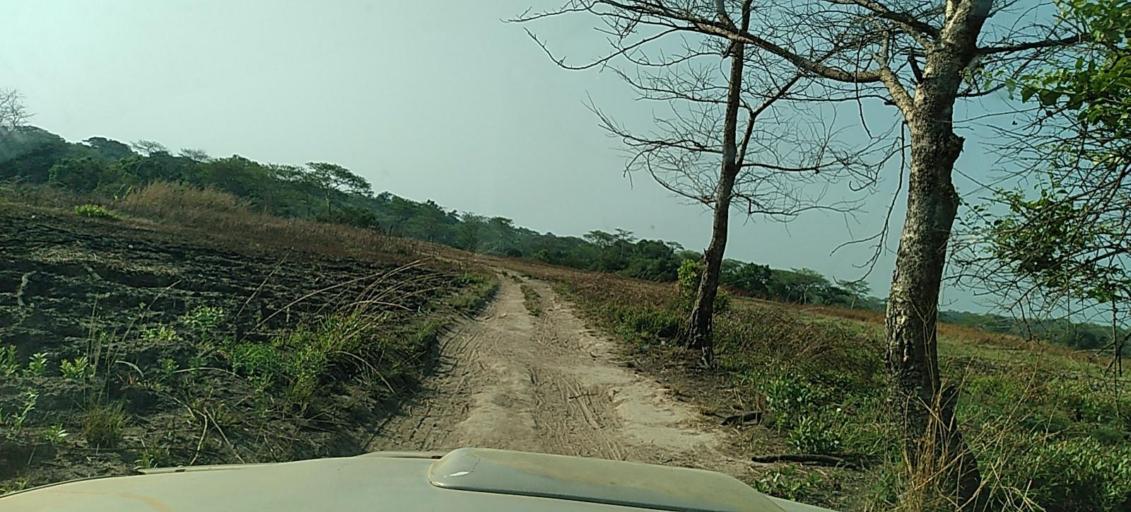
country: ZM
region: North-Western
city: Kasempa
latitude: -13.1898
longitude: 25.9695
